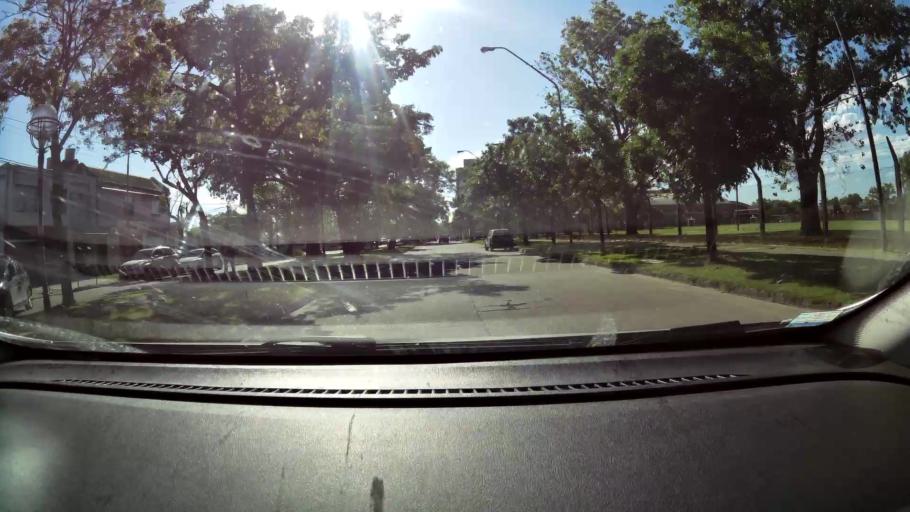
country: AR
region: Santa Fe
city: Santa Fe de la Vera Cruz
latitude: -31.6066
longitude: -60.6870
